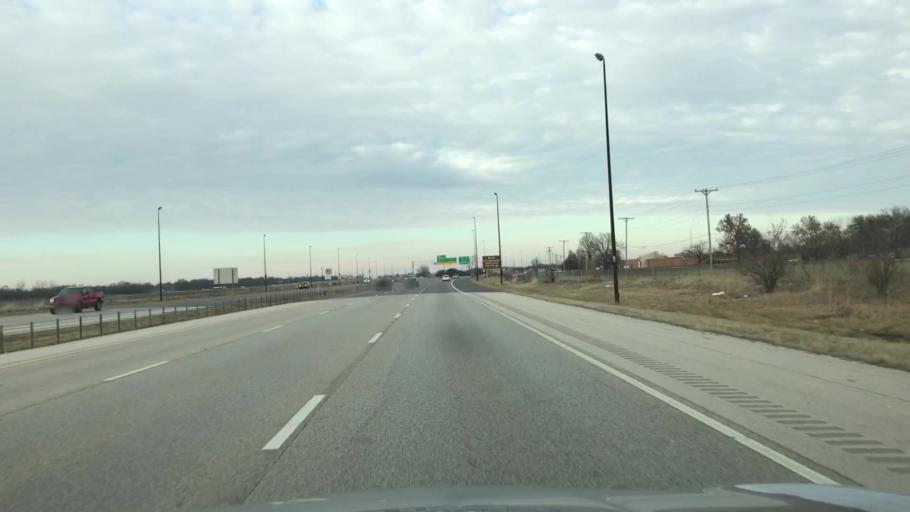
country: US
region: Illinois
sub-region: Sangamon County
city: Southern View
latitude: 39.7308
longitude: -89.6442
